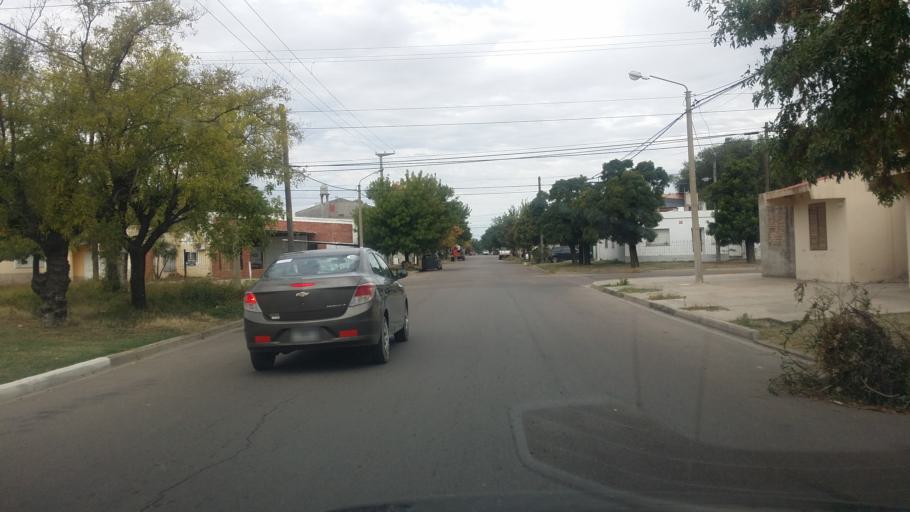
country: AR
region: La Pampa
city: Santa Rosa
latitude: -36.6351
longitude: -64.2884
